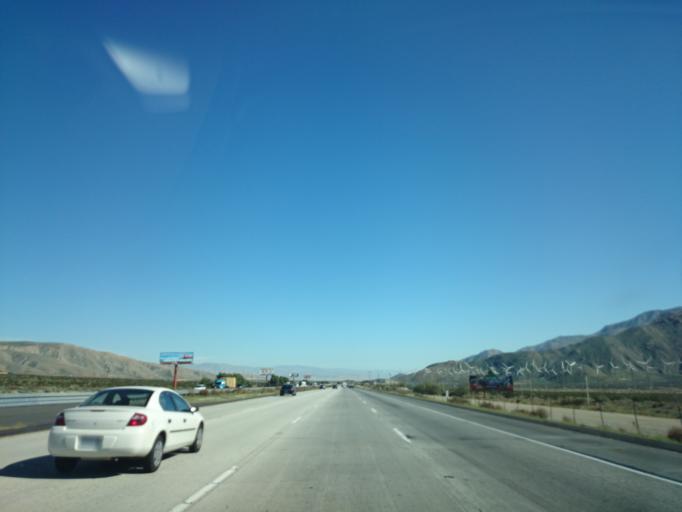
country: US
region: California
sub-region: Riverside County
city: Cabazon
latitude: 33.9243
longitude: -116.7325
